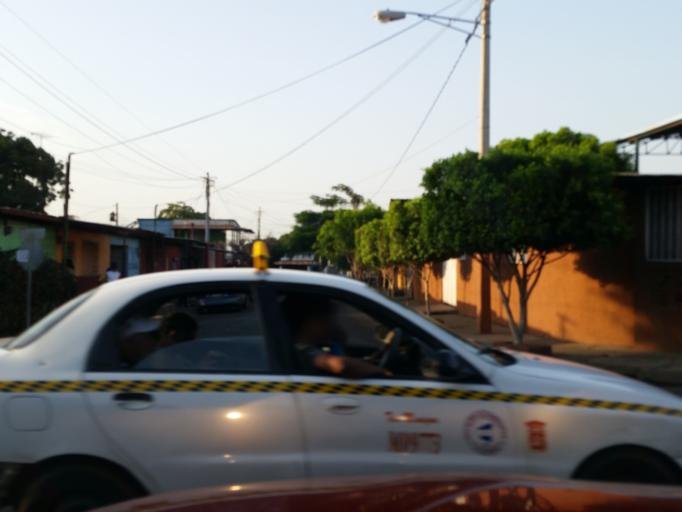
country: NI
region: Managua
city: Managua
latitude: 12.1418
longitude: -86.2539
